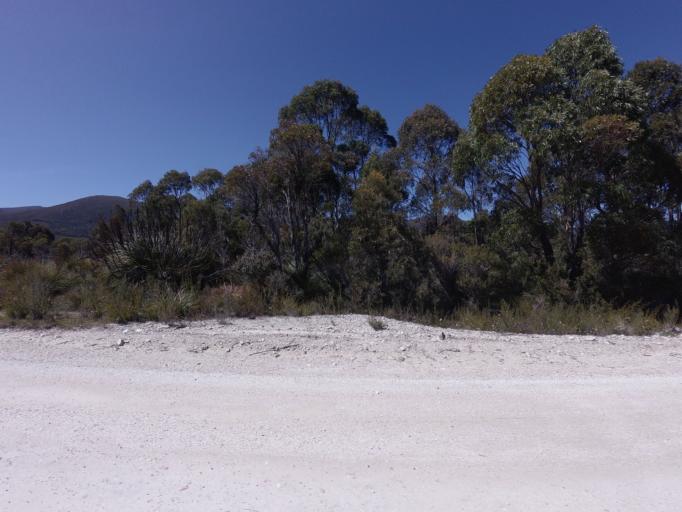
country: AU
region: Tasmania
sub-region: Huon Valley
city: Geeveston
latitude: -43.0269
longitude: 146.3532
